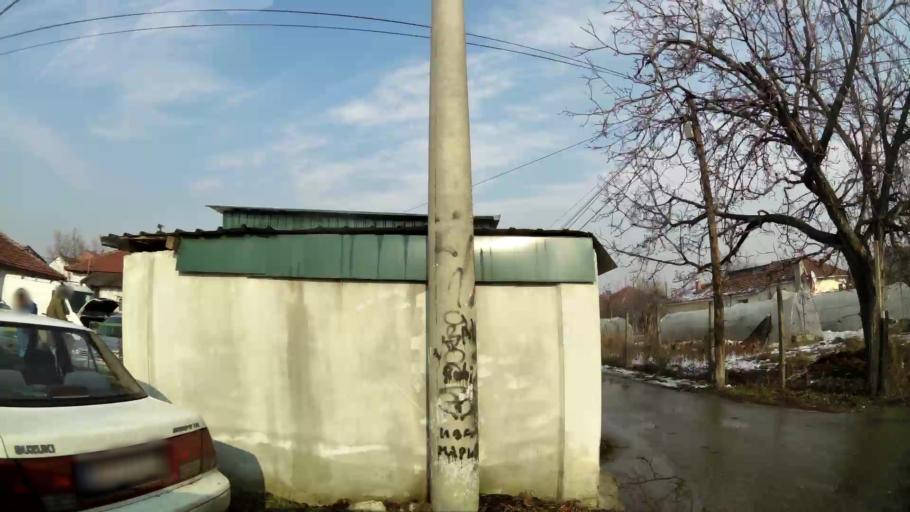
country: MK
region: Kisela Voda
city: Kisela Voda
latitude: 41.9921
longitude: 21.4984
